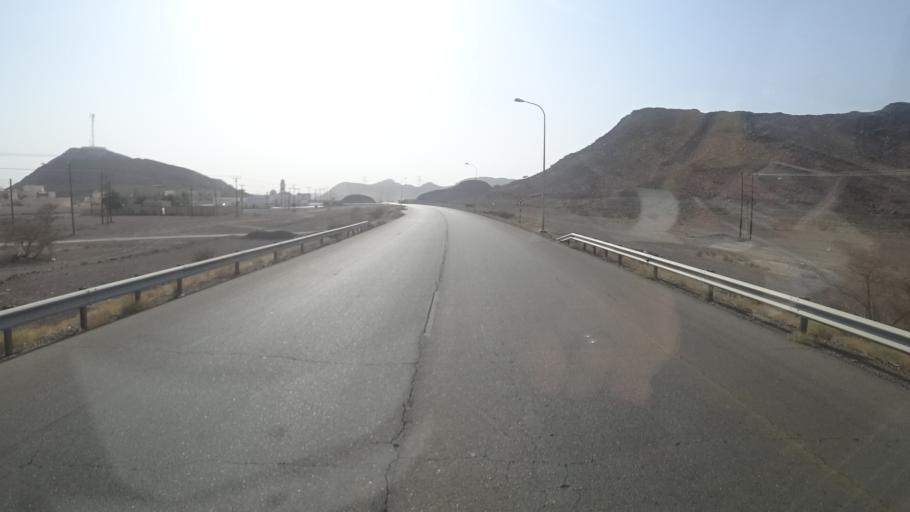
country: OM
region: Muhafazat ad Dakhiliyah
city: Izki
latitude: 22.7924
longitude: 57.8064
